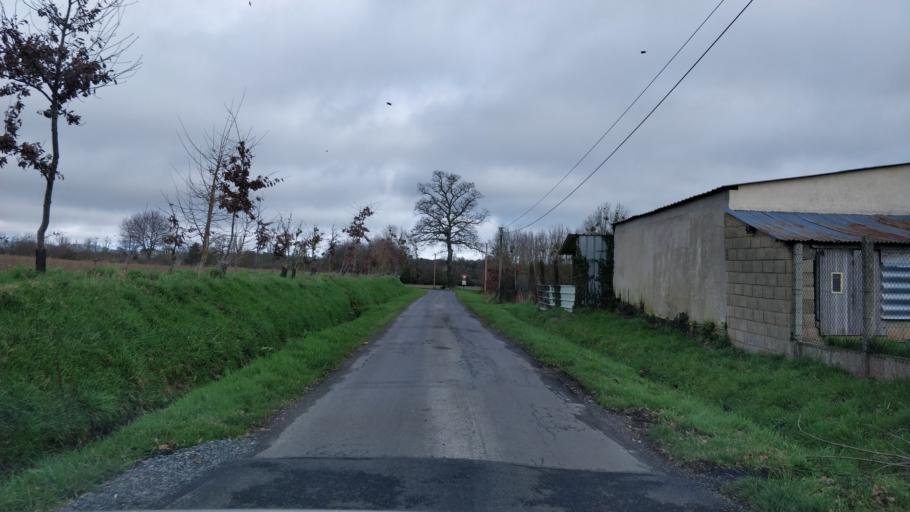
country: FR
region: Brittany
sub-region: Departement des Cotes-d'Armor
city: Lamballe
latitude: 48.4718
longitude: -2.5248
